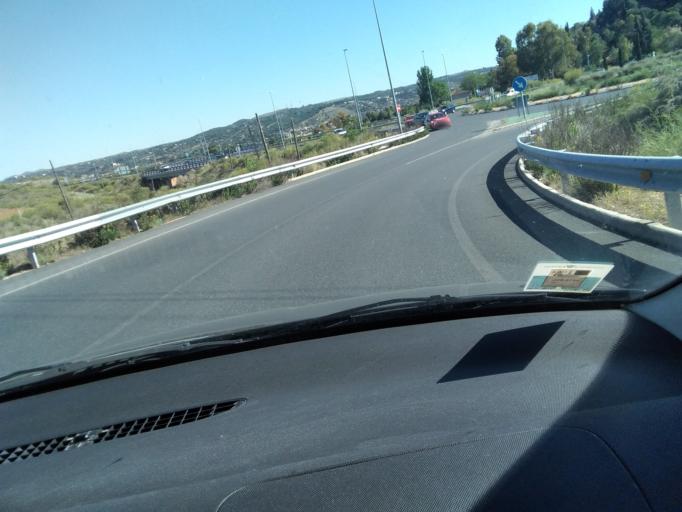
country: ES
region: Castille-La Mancha
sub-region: Province of Toledo
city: Toledo
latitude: 39.8864
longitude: -4.0544
